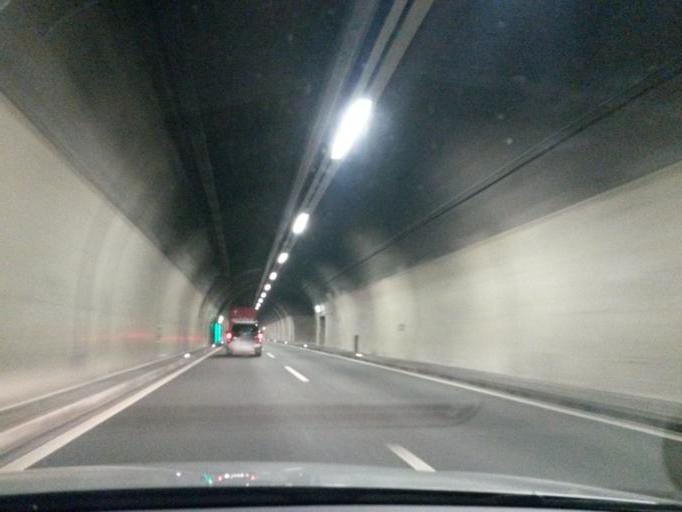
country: CH
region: Ticino
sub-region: Bellinzona District
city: Cadenazzo
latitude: 46.1330
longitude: 8.9201
